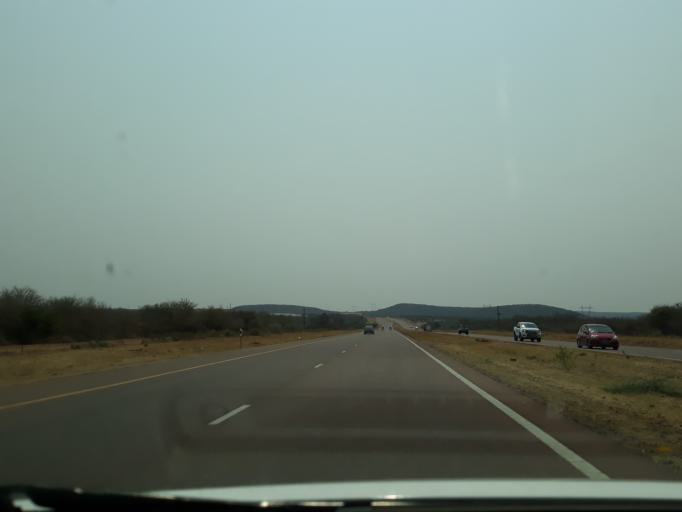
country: BW
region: Kgatleng
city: Bokaa
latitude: -24.4097
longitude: 26.0521
